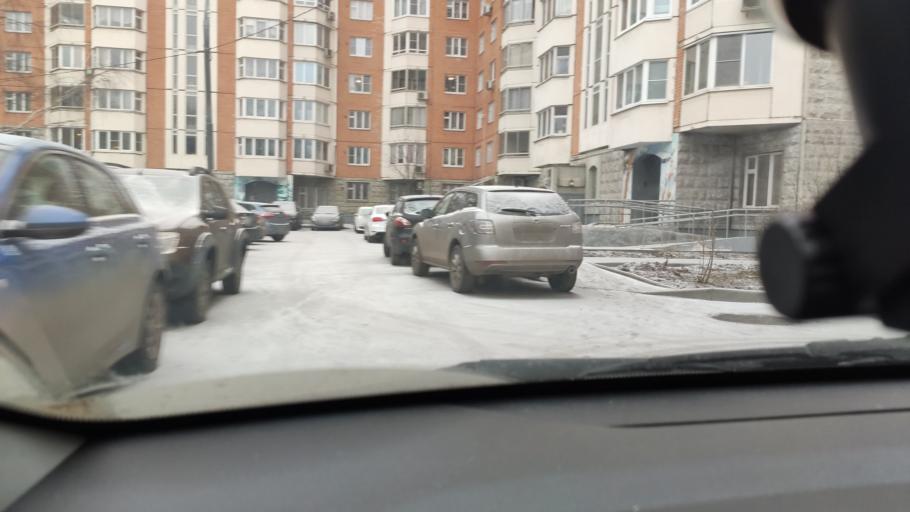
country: RU
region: Moscow
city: Annino
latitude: 55.5912
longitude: 37.6125
